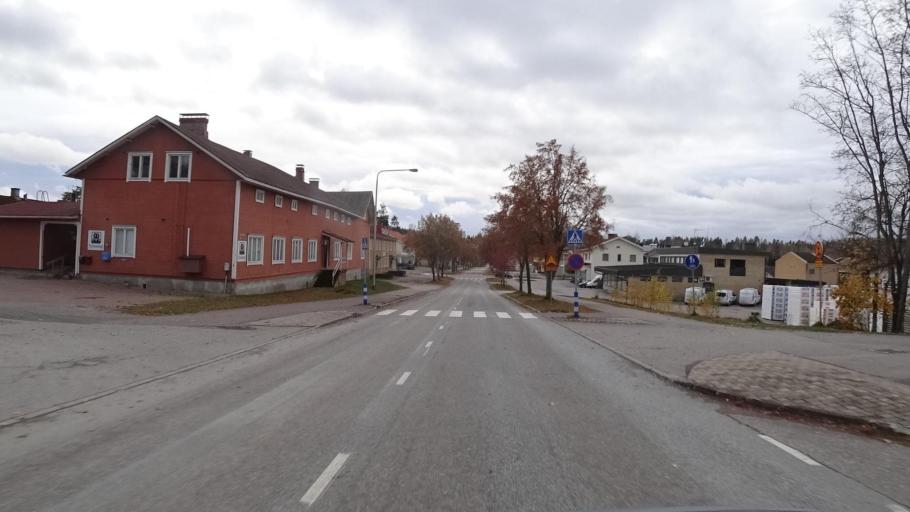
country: FI
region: Central Finland
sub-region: Joutsa
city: Joutsa
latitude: 61.7413
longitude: 26.1139
